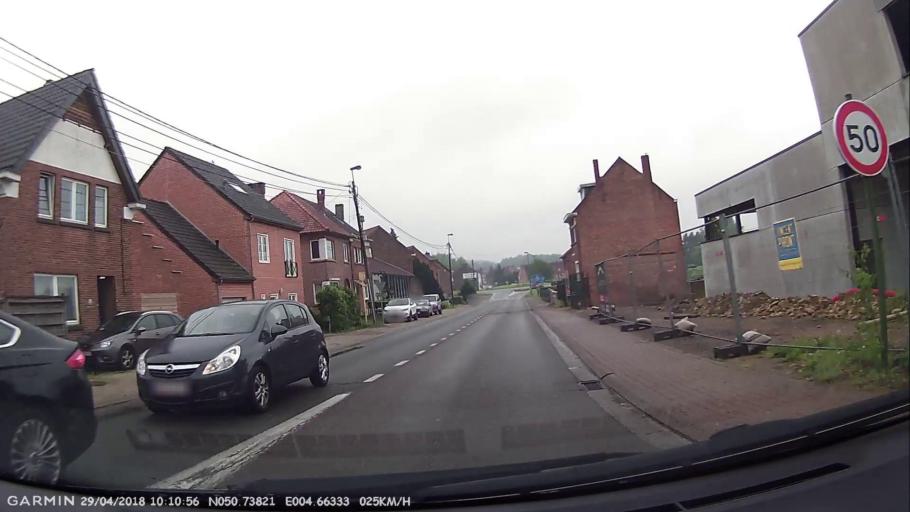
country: BE
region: Wallonia
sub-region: Province du Brabant Wallon
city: Grez-Doiceau
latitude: 50.7384
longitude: 4.6636
